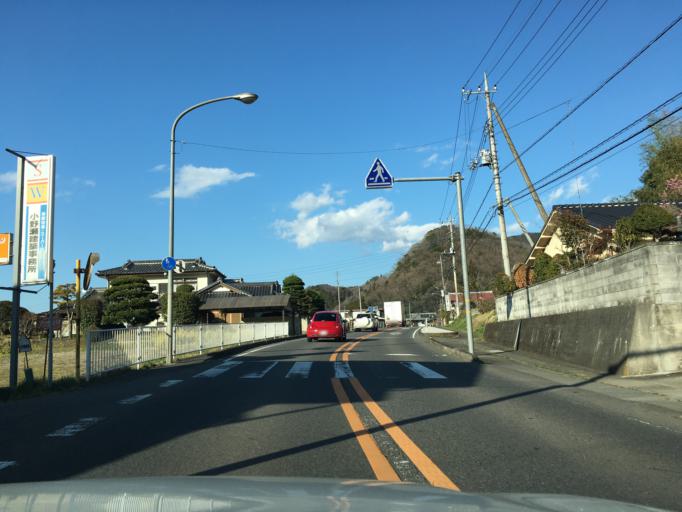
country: JP
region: Ibaraki
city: Daigo
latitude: 36.7089
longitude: 140.3841
